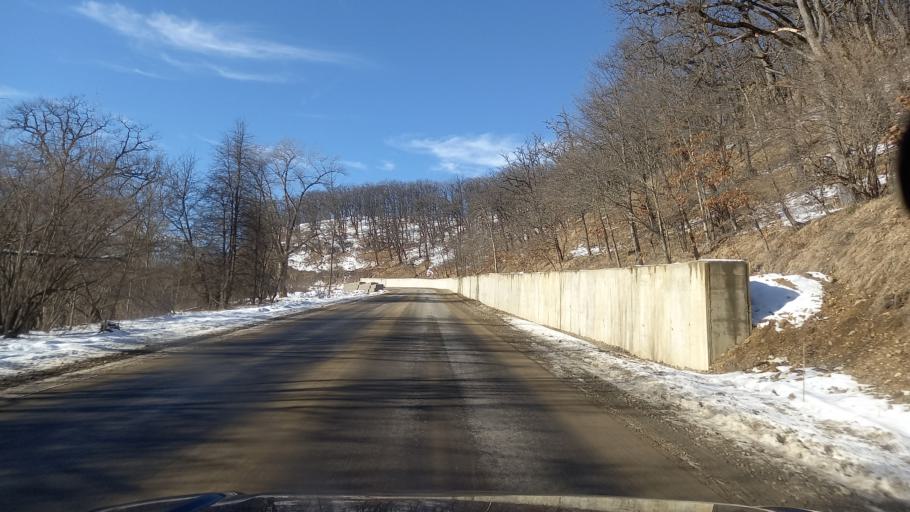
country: RU
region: Adygeya
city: Kamennomostskiy
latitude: 44.2385
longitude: 40.1632
